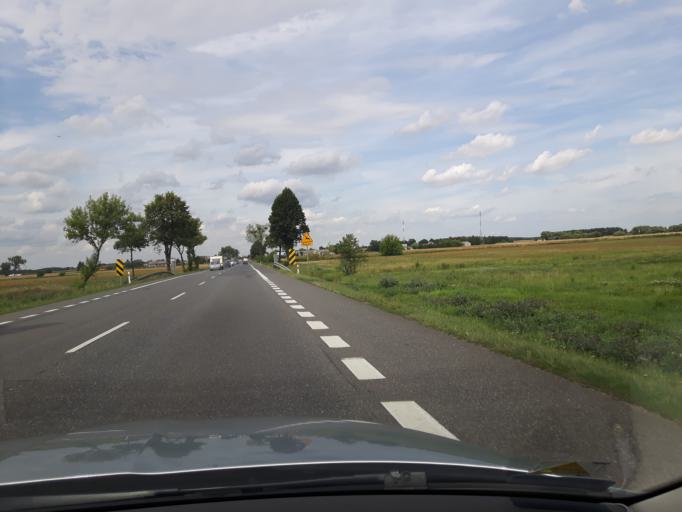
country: PL
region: Masovian Voivodeship
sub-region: Powiat mlawski
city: Strzegowo
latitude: 52.9339
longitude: 20.2846
